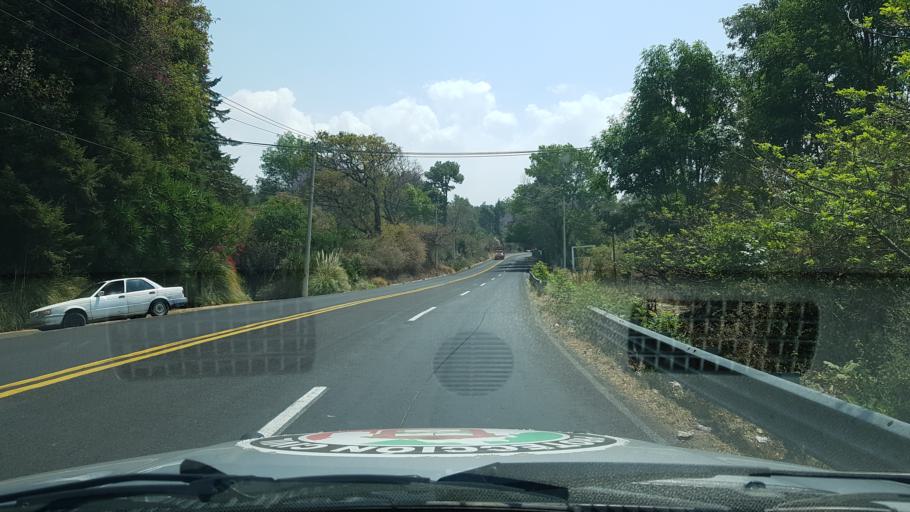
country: MX
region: Mexico
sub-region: Tepetlixpa
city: Nepantla de Sor Juana Ines de la Cruz
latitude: 18.9891
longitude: -98.8329
